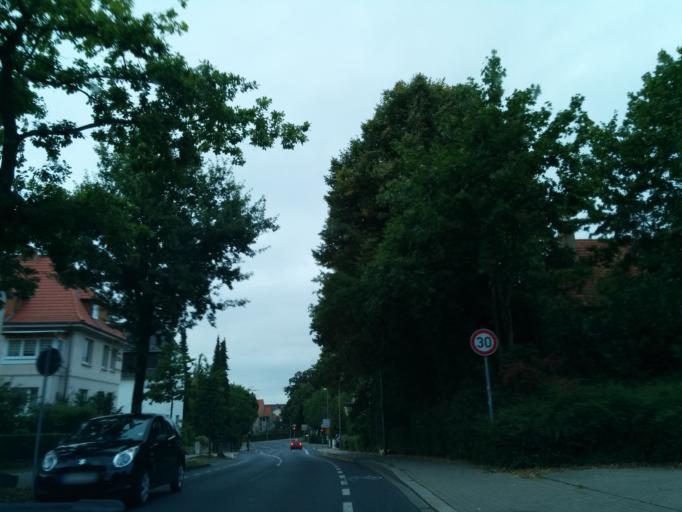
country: DE
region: Lower Saxony
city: Goettingen
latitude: 51.5416
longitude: 9.9499
